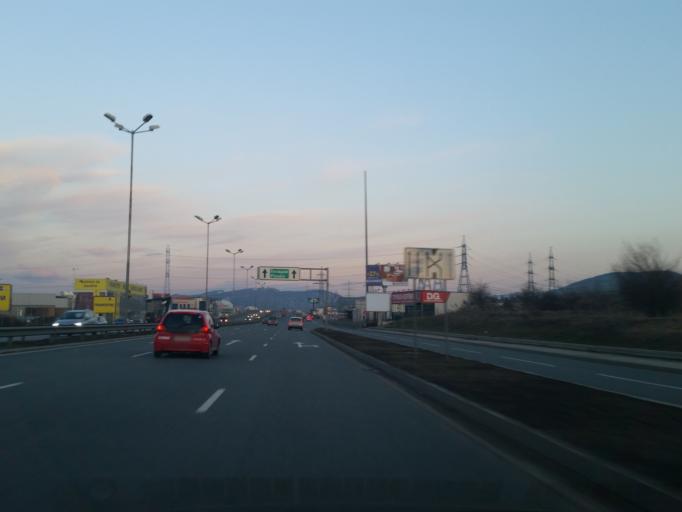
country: BG
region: Sofia-Capital
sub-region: Stolichna Obshtina
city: Sofia
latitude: 42.6352
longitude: 23.3279
